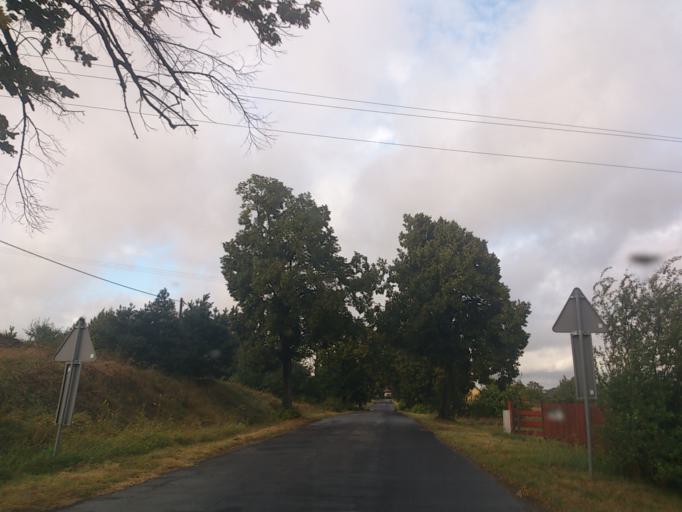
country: PL
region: Greater Poland Voivodeship
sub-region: Powiat poznanski
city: Pobiedziska
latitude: 52.4922
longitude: 17.3636
